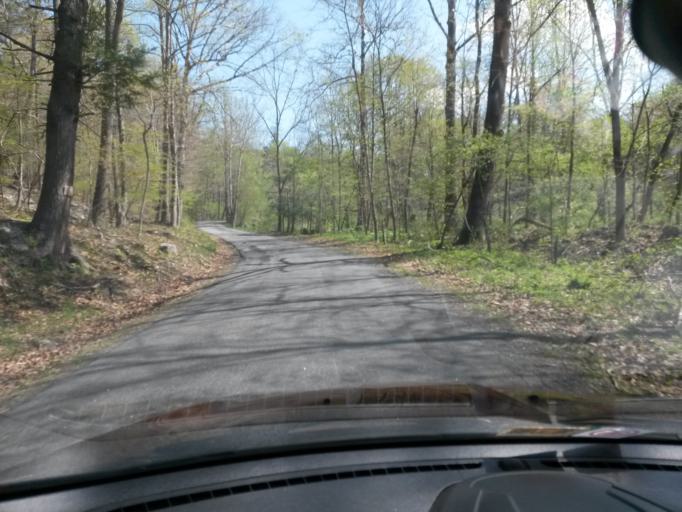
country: US
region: Virginia
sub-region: Bath County
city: Warm Springs
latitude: 38.2176
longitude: -79.6731
